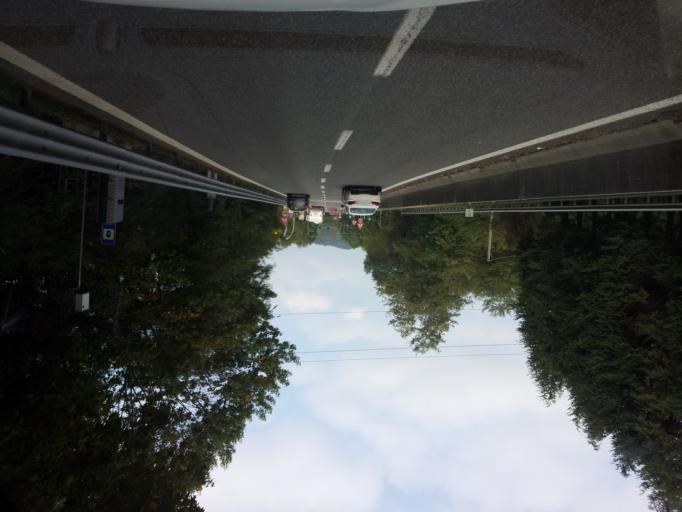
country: IT
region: Lombardy
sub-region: Provincia di Varese
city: Corgeno
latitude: 45.7352
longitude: 8.6796
